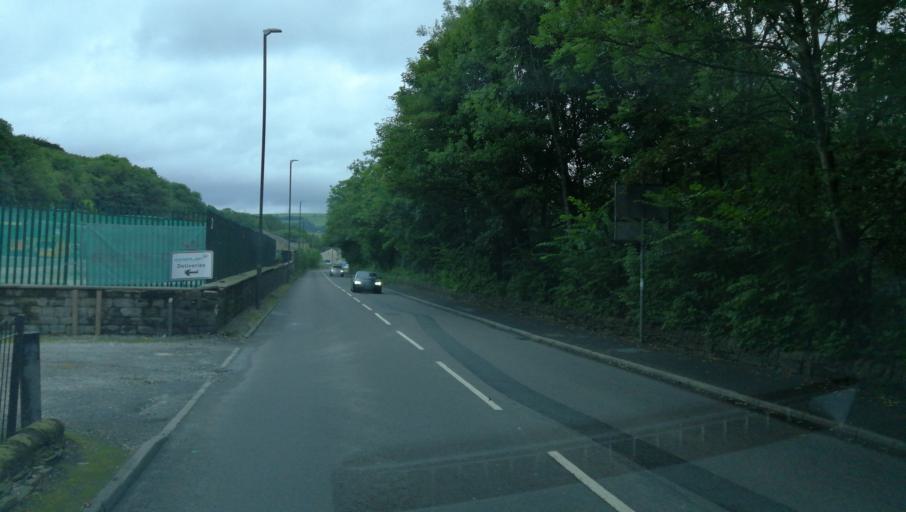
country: GB
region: England
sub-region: Derbyshire
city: Glossop
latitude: 53.4478
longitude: -1.9755
